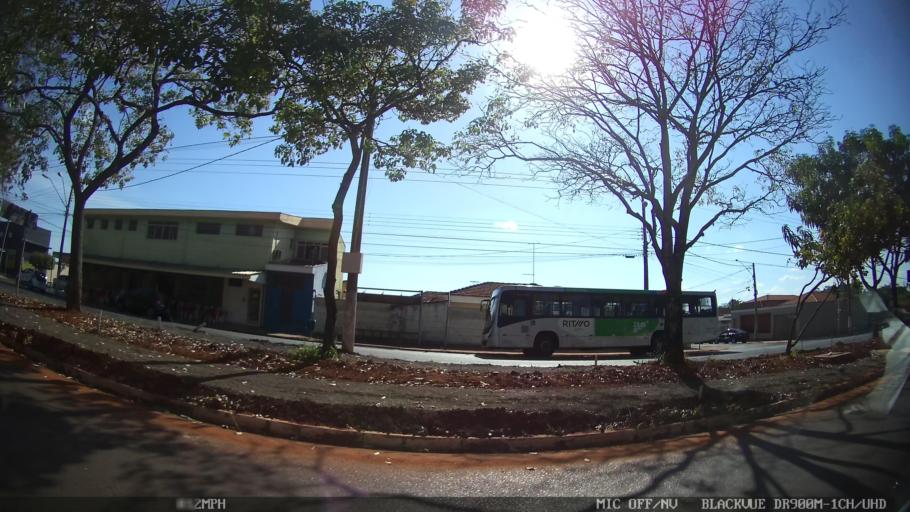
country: BR
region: Sao Paulo
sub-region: Ribeirao Preto
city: Ribeirao Preto
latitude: -21.1563
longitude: -47.7840
